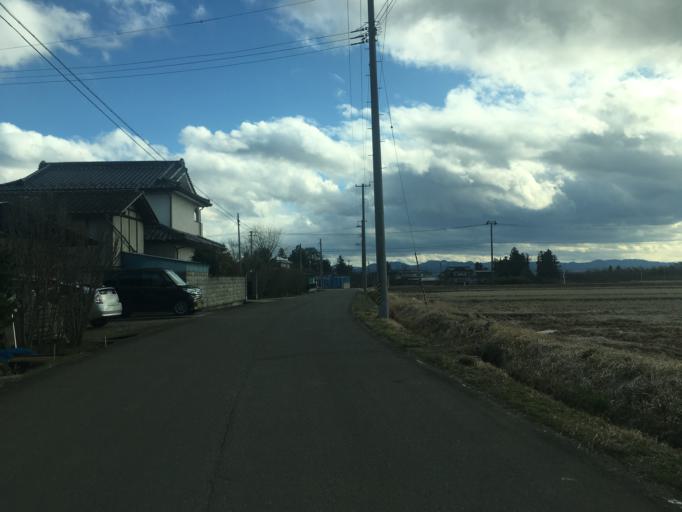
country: JP
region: Fukushima
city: Yanagawamachi-saiwaicho
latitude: 37.8782
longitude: 140.5878
